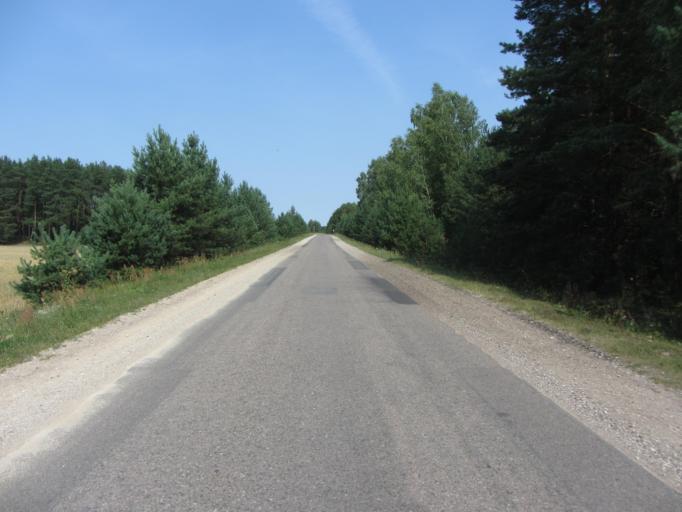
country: LT
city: Veisiejai
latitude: 54.0442
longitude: 23.6553
